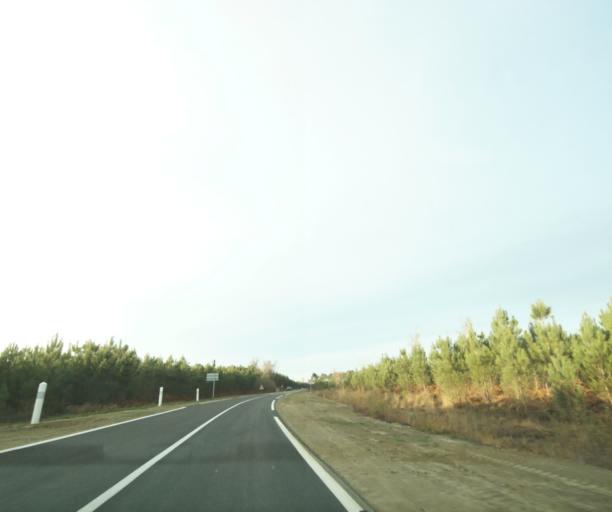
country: FR
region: Aquitaine
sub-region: Departement des Landes
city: Gabarret
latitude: 44.0865
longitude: -0.0934
